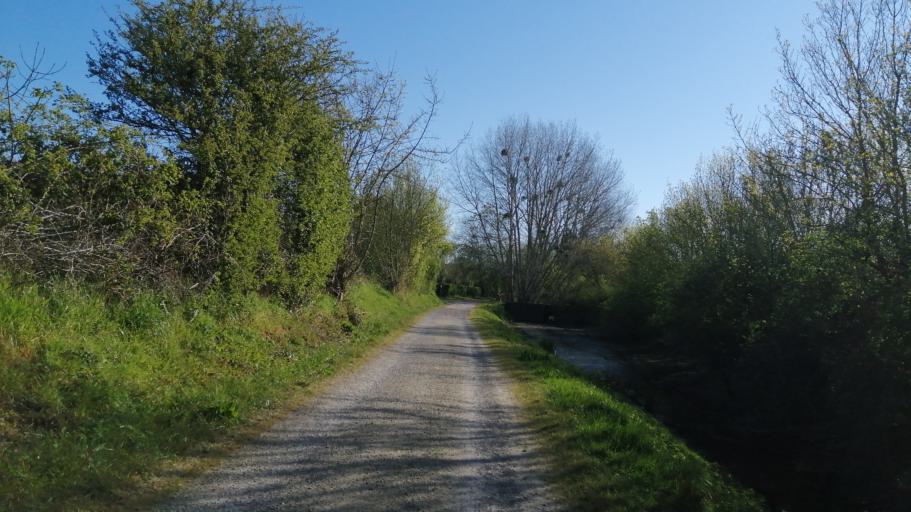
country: FR
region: Pays de la Loire
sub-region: Departement de la Loire-Atlantique
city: Saint-Gereon
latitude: 47.3613
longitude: -1.1968
